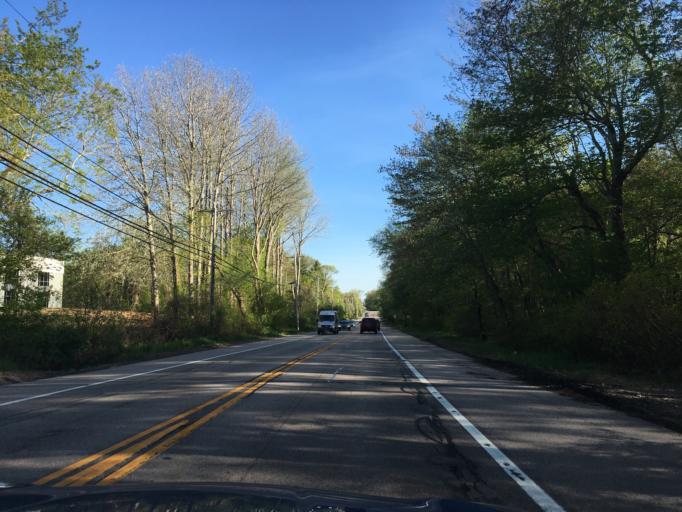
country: US
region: Rhode Island
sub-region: Kent County
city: East Greenwich
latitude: 41.6431
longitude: -71.4952
